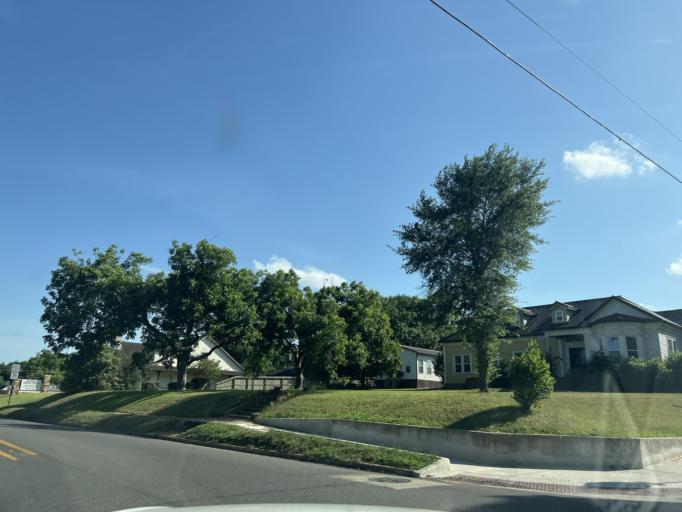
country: US
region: Texas
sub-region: Washington County
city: Brenham
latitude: 30.1562
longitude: -96.3986
